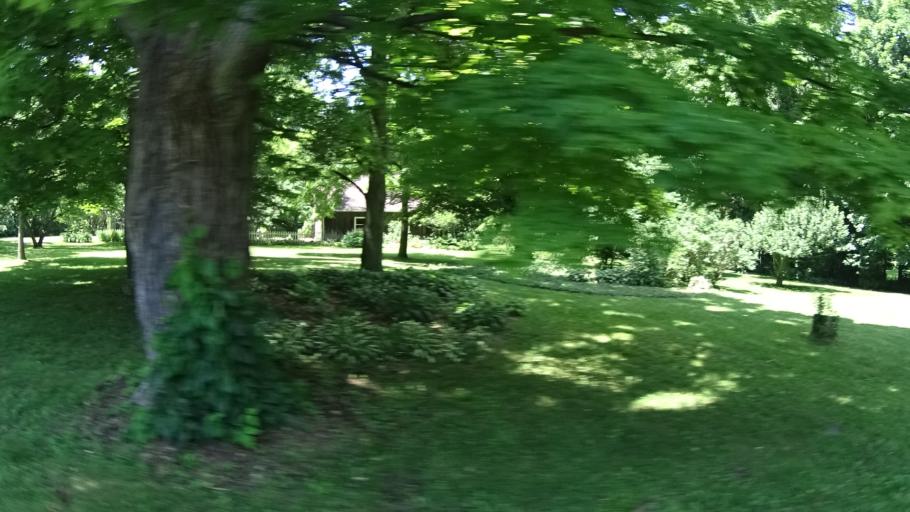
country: US
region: Ohio
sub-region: Lorain County
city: Vermilion
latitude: 41.3470
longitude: -82.4005
